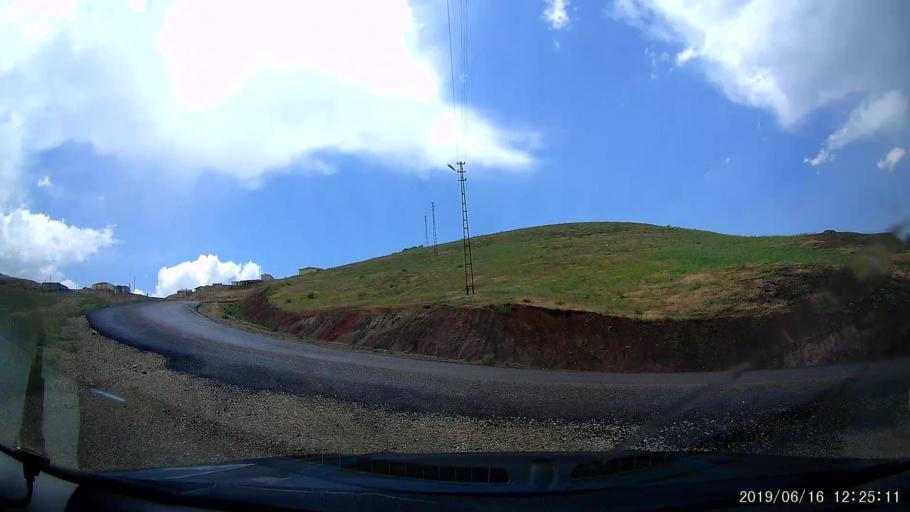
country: TR
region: Agri
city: Dogubayazit
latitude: 39.4427
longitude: 44.2336
